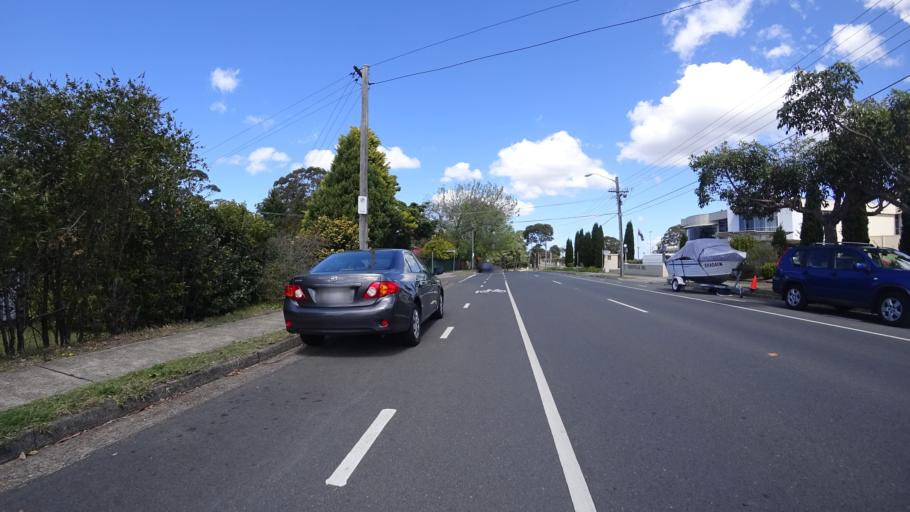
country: AU
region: New South Wales
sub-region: Warringah
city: Forestville
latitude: -33.7622
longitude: 151.2114
